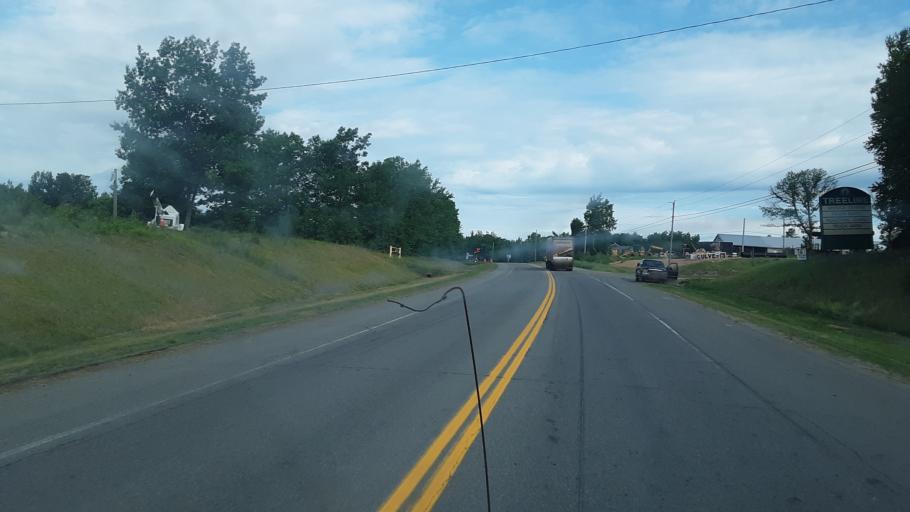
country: US
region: Maine
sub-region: Penobscot County
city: Lincoln
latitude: 45.3687
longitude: -68.5546
